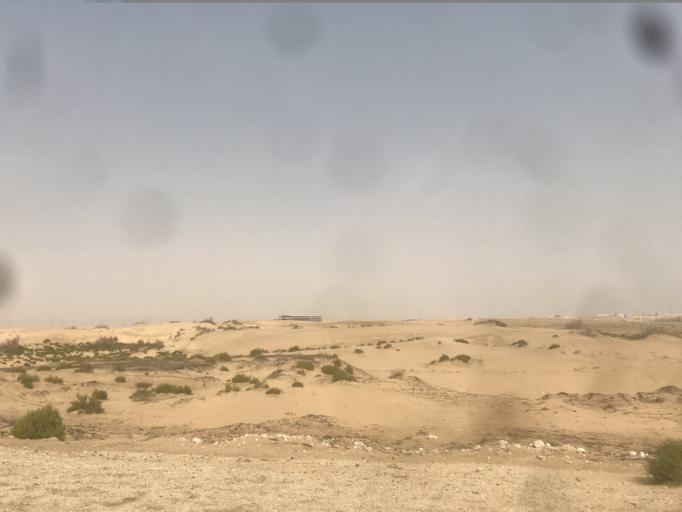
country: SA
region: Eastern Province
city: Abqaiq
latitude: 25.9086
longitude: 49.9276
